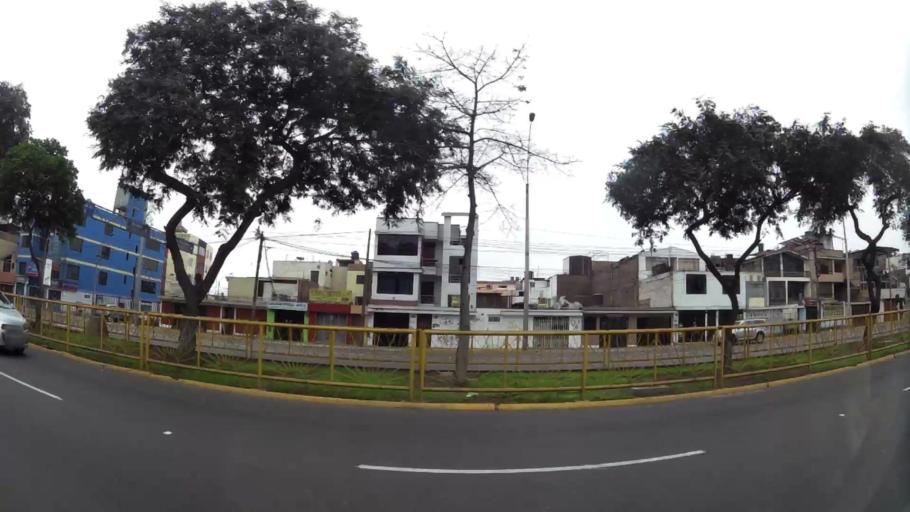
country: PE
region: Lima
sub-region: Lima
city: San Luis
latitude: -12.0796
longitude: -76.9913
